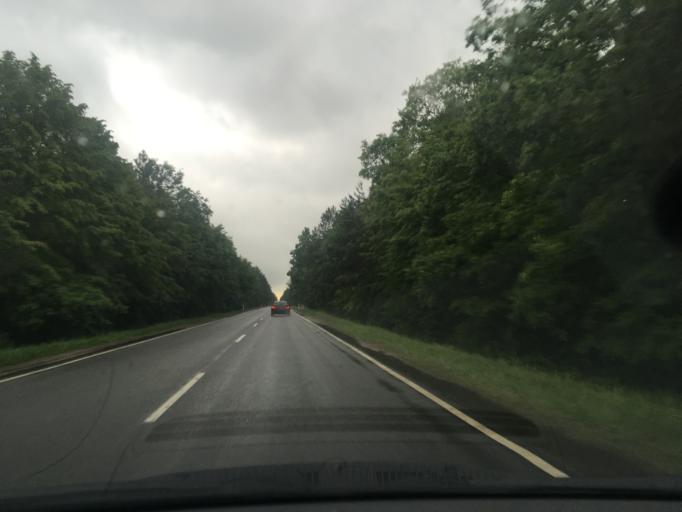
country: PL
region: Lublin Voivodeship
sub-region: Powiat rycki
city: Ryki
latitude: 51.5826
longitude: 21.9198
